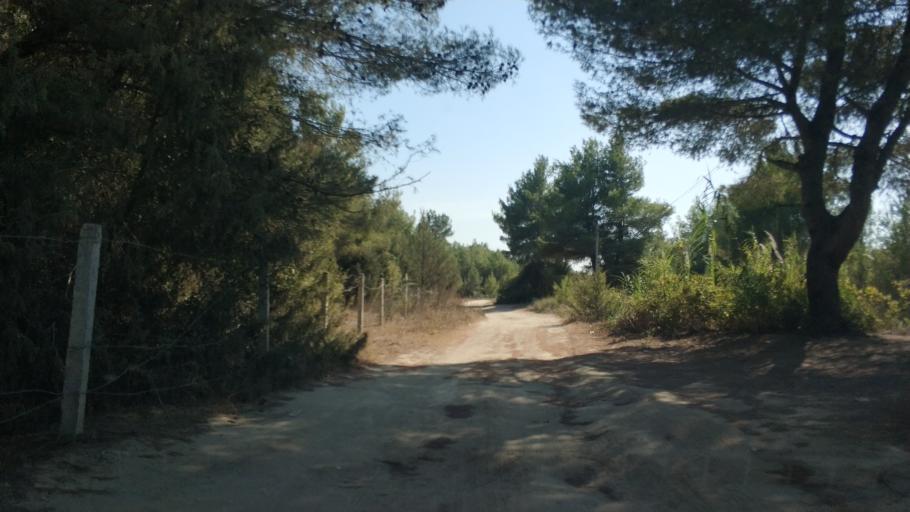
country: AL
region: Fier
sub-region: Rrethi i Lushnjes
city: Divjake
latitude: 40.9630
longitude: 19.4767
